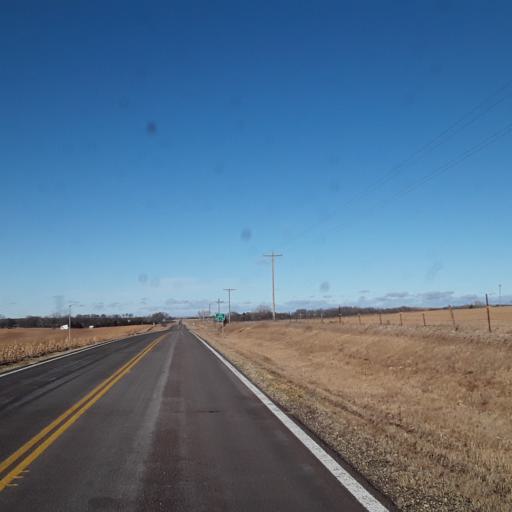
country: US
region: Kansas
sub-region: Cloud County
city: Concordia
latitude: 39.5085
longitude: -97.7228
